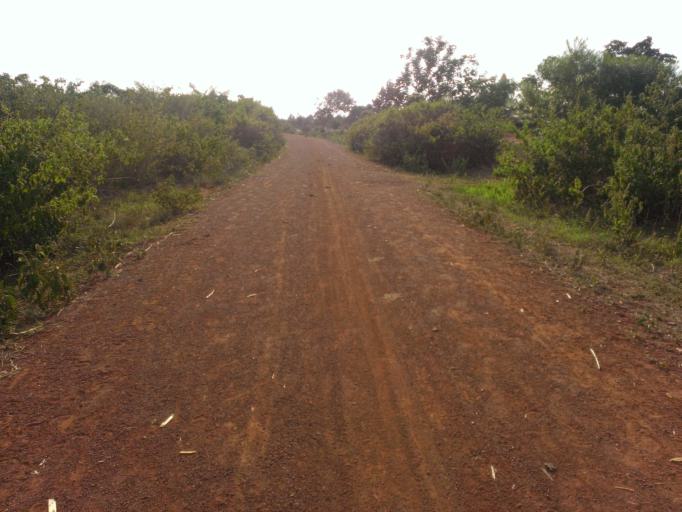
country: UG
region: Eastern Region
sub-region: Busia District
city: Busia
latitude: 0.5506
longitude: 33.9904
